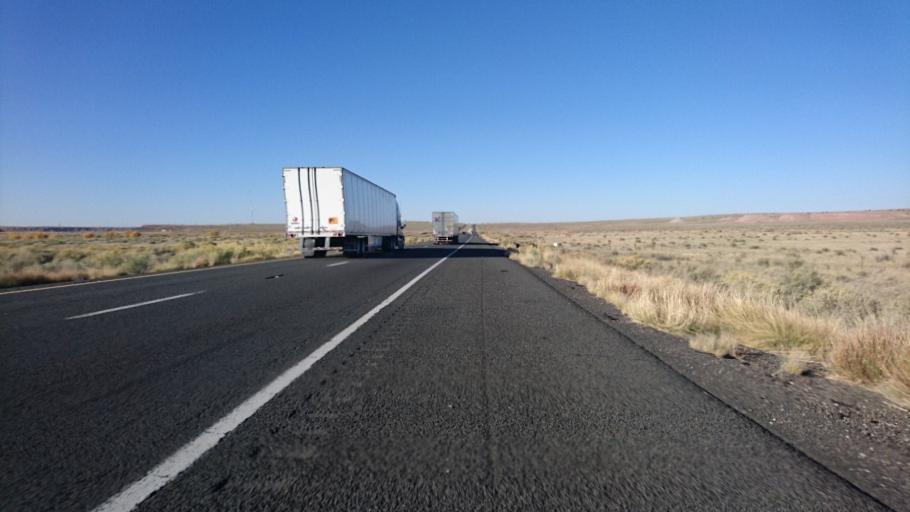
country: US
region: Arizona
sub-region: Apache County
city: Houck
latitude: 35.1136
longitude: -109.5844
